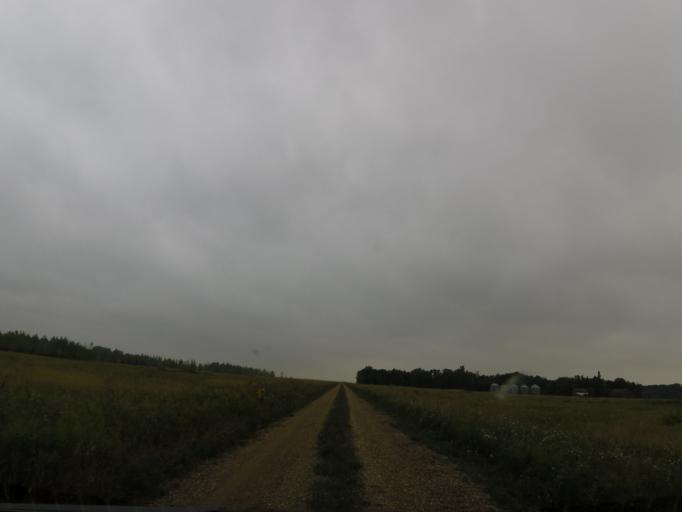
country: US
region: North Dakota
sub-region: Walsh County
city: Grafton
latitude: 48.4213
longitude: -97.1181
